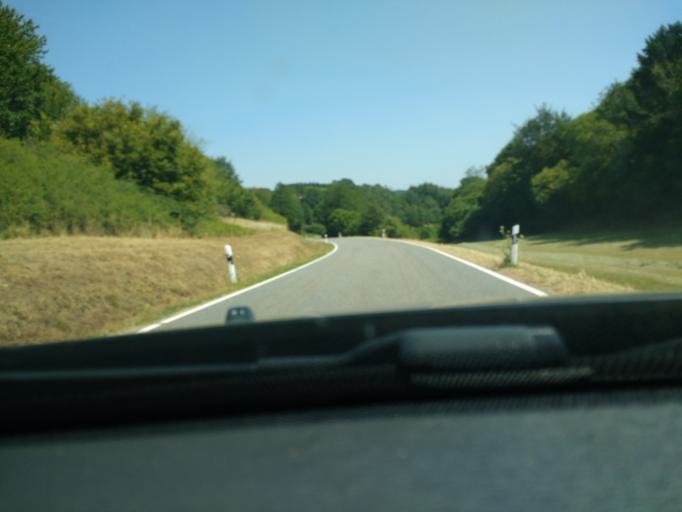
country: DE
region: Rheinland-Pfalz
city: Bettenfeld
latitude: 50.0896
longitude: 6.7756
